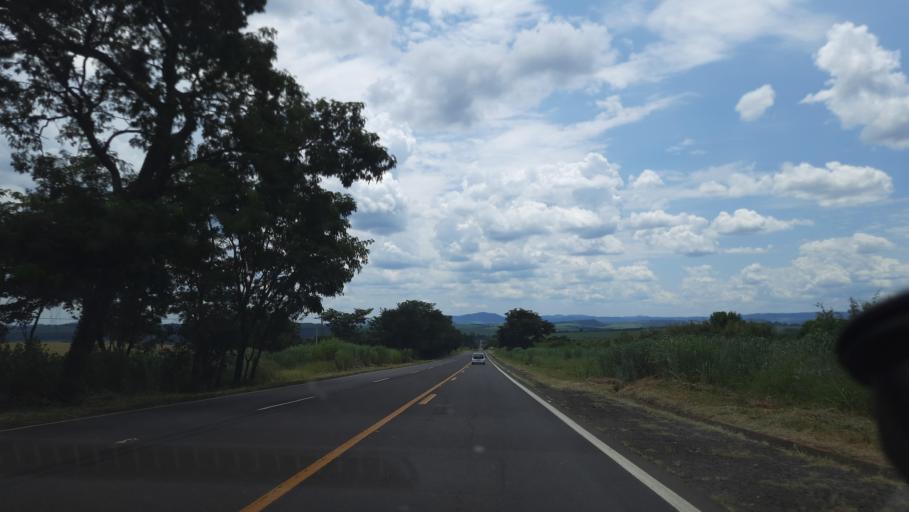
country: BR
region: Sao Paulo
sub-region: Mococa
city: Mococa
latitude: -21.4851
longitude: -47.0815
